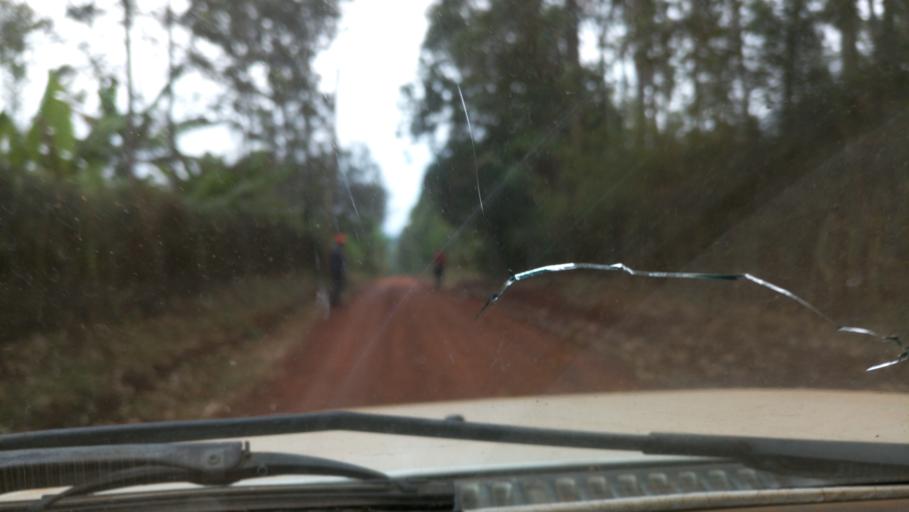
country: KE
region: Murang'a District
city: Maragua
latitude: -0.8408
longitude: 37.1545
